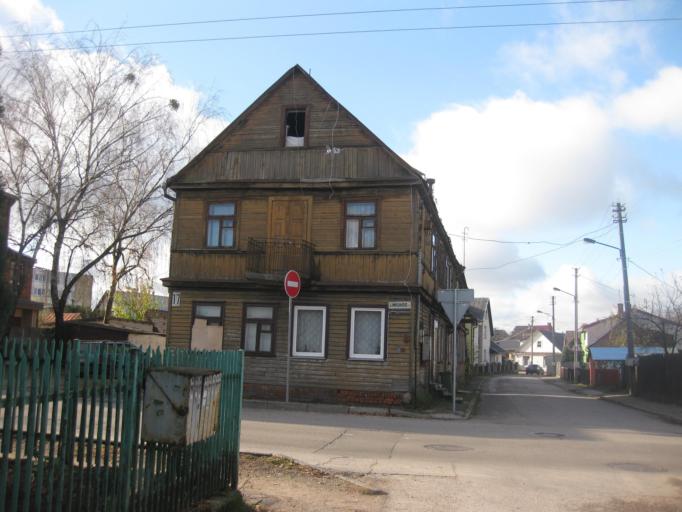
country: LT
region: Kauno apskritis
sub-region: Kaunas
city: Kaunas
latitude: 54.9082
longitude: 23.8902
